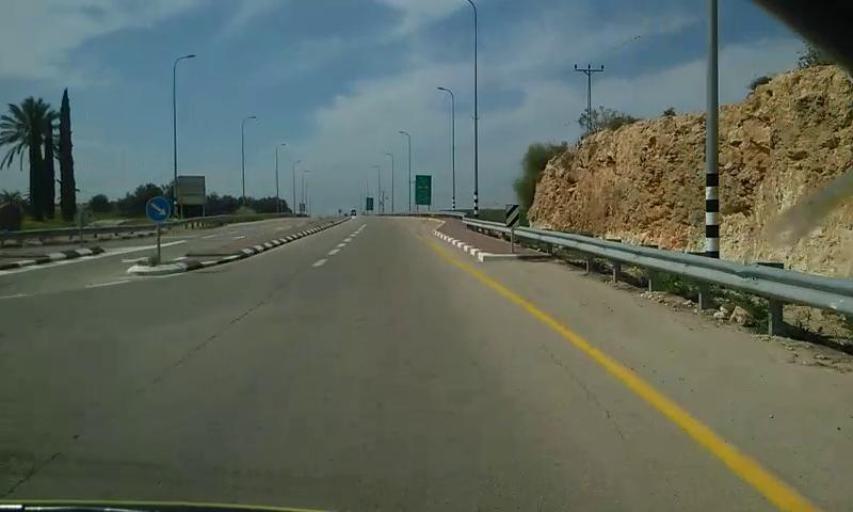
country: PS
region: West Bank
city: Az Zahiriyah
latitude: 31.3759
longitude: 35.0070
